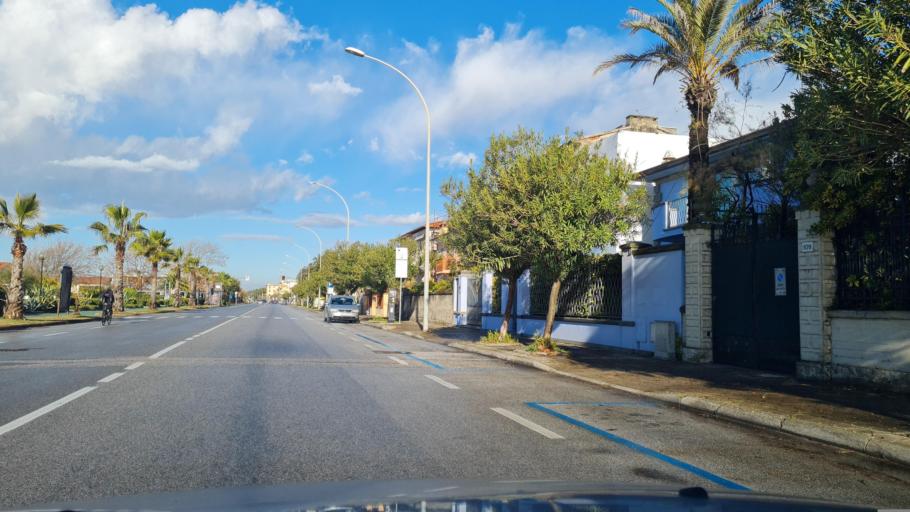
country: IT
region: Tuscany
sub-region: Provincia di Lucca
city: Pietrasanta
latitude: 43.9343
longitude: 10.1925
